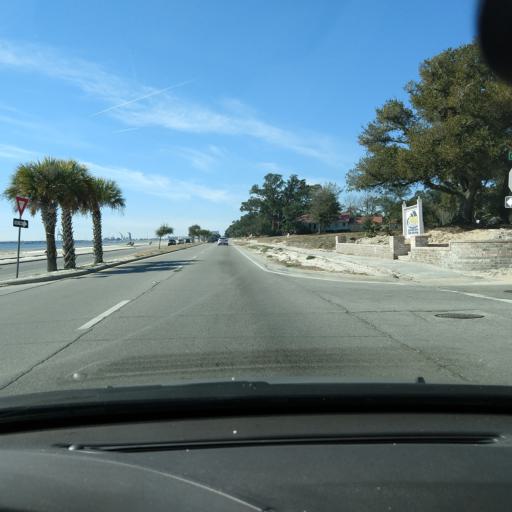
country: US
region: Mississippi
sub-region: Harrison County
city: Gulfport
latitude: 30.3743
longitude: -89.0649
